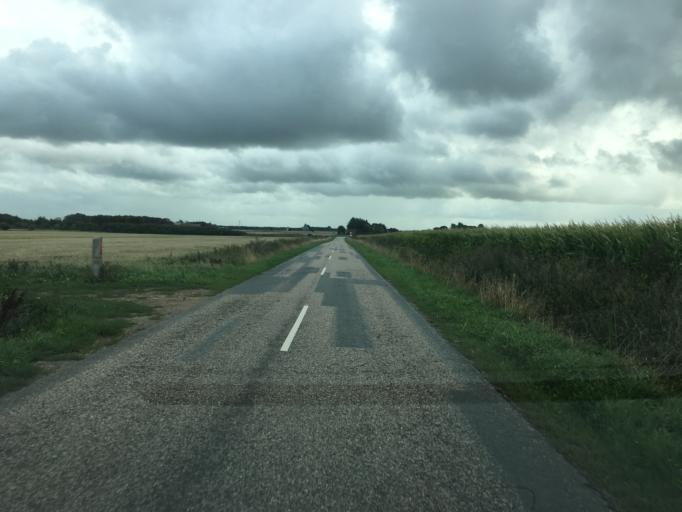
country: DK
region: South Denmark
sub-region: Tonder Kommune
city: Tonder
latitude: 54.9528
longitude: 8.8236
